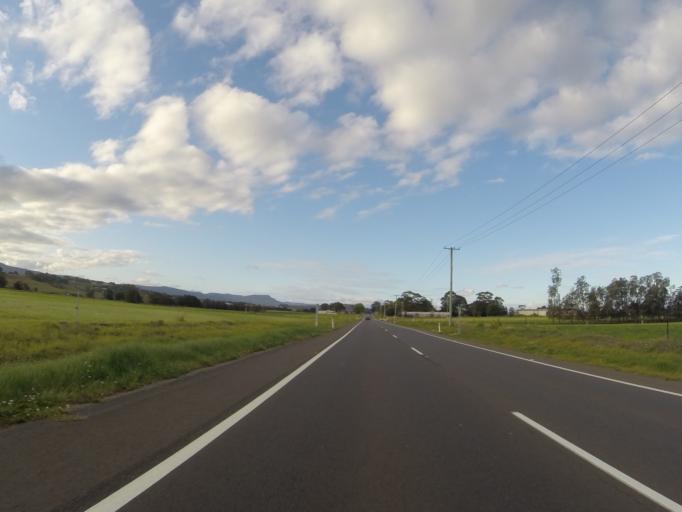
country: AU
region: New South Wales
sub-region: Shellharbour
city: Albion Park Rail
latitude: -34.5565
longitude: 150.7802
